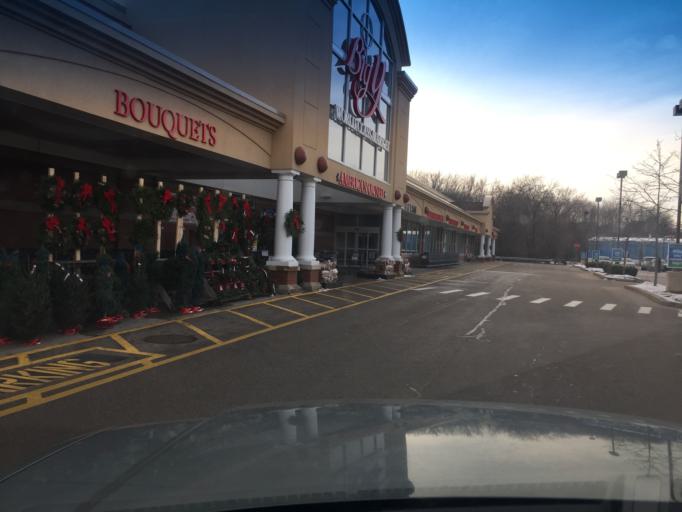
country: US
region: Massachusetts
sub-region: Norfolk County
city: Franklin
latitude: 42.0793
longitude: -71.3804
